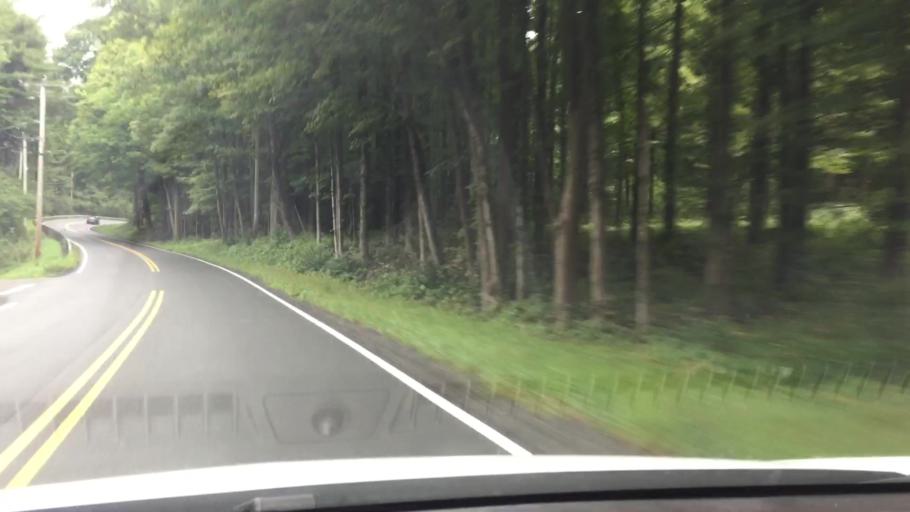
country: US
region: Massachusetts
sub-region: Berkshire County
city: Housatonic
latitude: 42.2983
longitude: -73.3749
